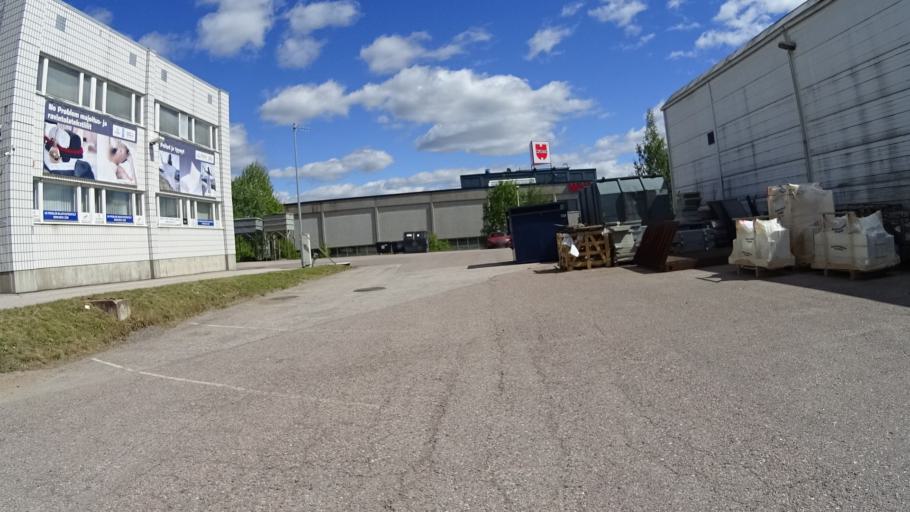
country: FI
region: Uusimaa
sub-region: Helsinki
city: Espoo
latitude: 60.2155
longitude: 24.6504
